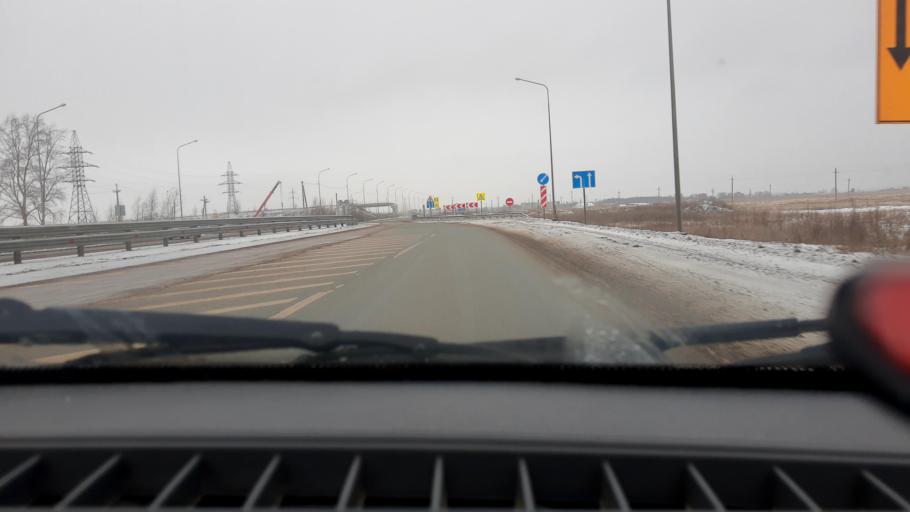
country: RU
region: Bashkortostan
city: Asanovo
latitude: 54.8992
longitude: 55.6338
